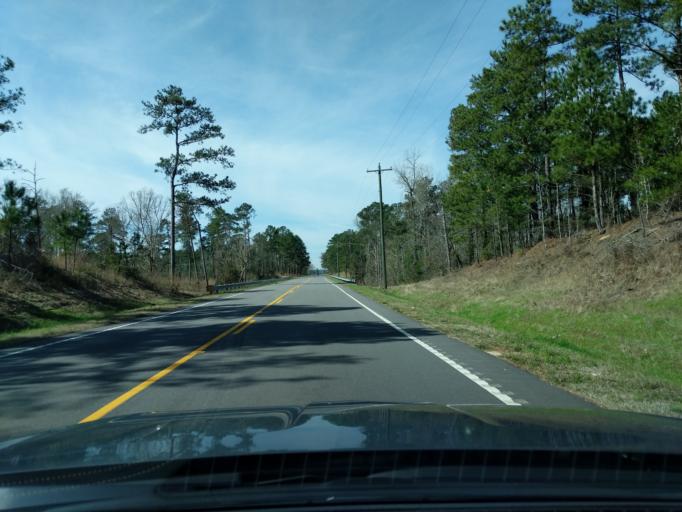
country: US
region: Georgia
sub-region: Columbia County
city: Evans
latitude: 33.6725
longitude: -82.1794
